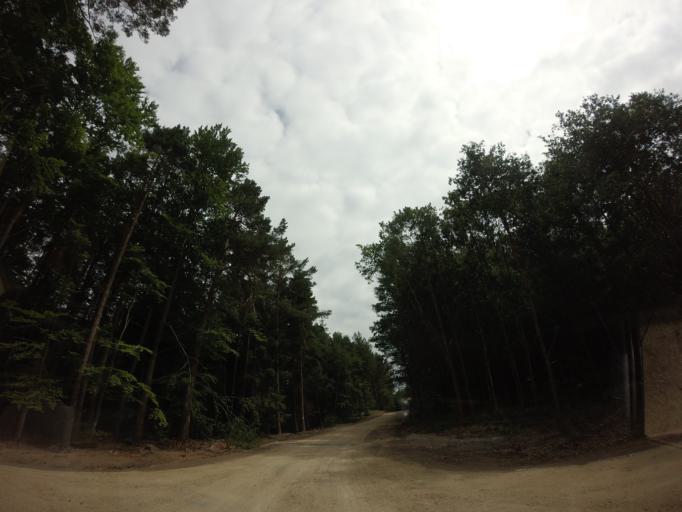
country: PL
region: Lubusz
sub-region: Powiat strzelecko-drezdenecki
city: Stare Kurowo
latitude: 52.8844
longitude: 15.6321
